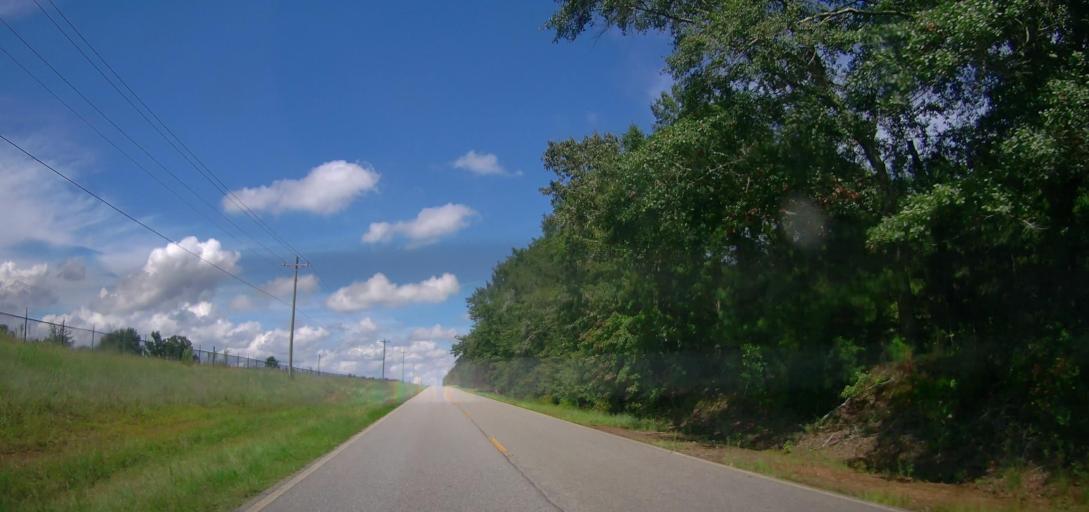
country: US
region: Georgia
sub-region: Peach County
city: Fort Valley
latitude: 32.5081
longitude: -83.8647
